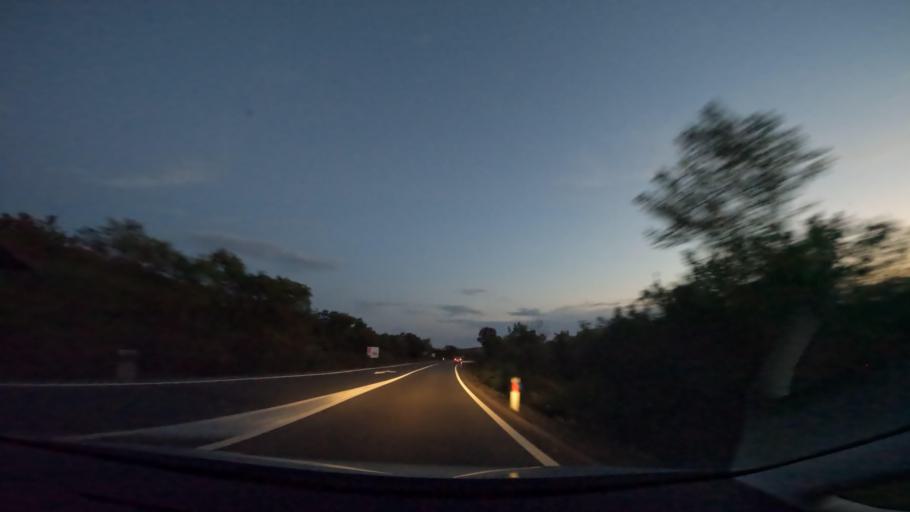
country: HR
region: Primorsko-Goranska
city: Omisalj
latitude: 45.1980
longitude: 14.5630
